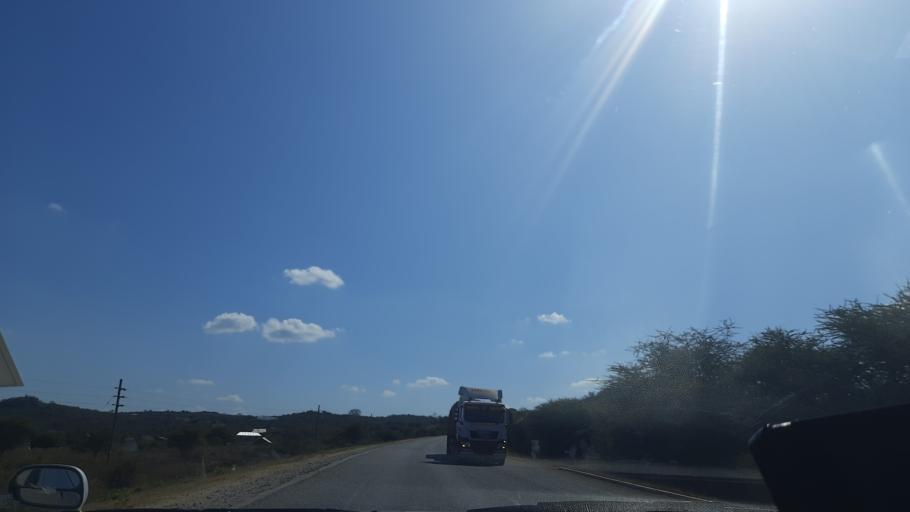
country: TZ
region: Singida
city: Kilimatinde
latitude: -5.7828
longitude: 34.8881
